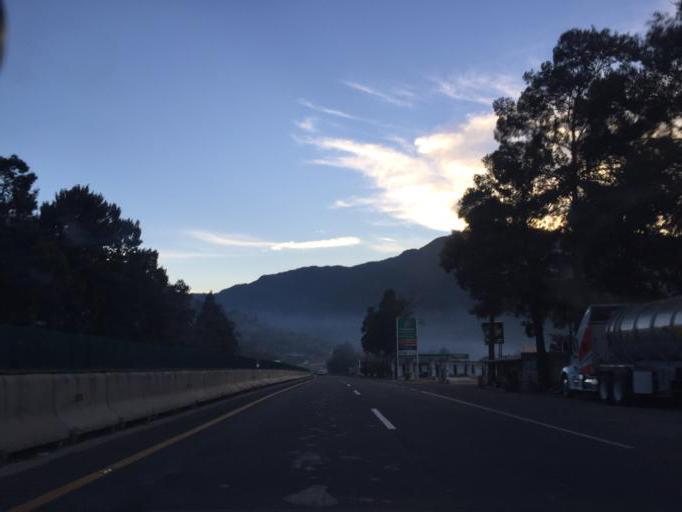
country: MX
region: Veracruz
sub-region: Nogales
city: Agricola Lazaro Cardenas
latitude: 18.8136
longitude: -97.1895
